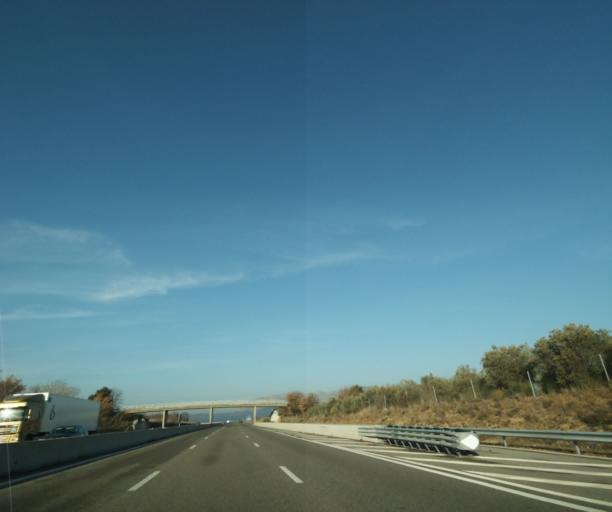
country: FR
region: Provence-Alpes-Cote d'Azur
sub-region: Departement du Var
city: Pourrieres
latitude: 43.4801
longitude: 5.7455
